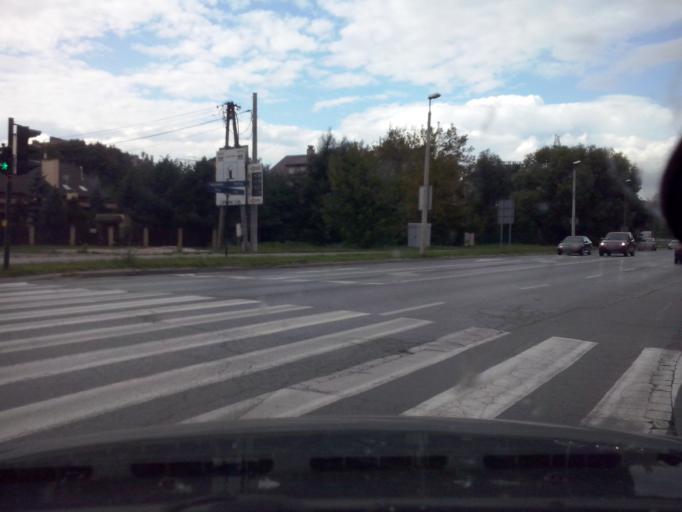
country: PL
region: Lesser Poland Voivodeship
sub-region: Krakow
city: Krakow
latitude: 50.0453
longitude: 19.9838
